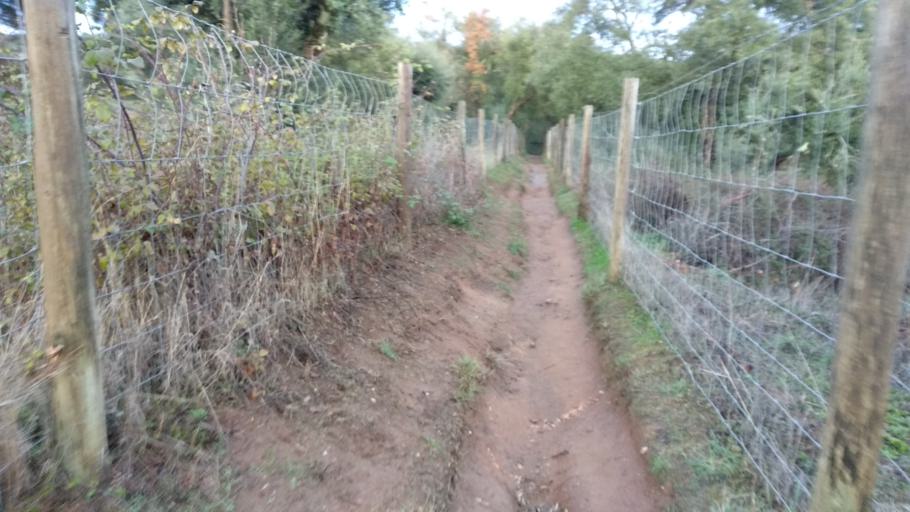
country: PT
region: Evora
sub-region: Evora
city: Evora
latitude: 38.5641
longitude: -8.0481
